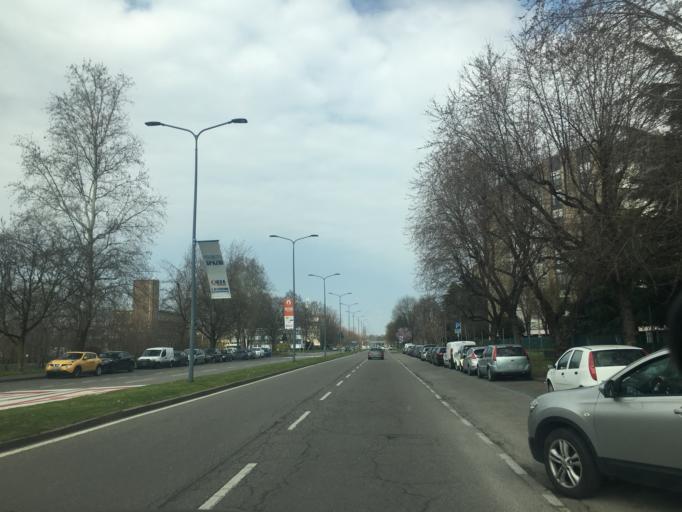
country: IT
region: Lombardy
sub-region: Citta metropolitana di Milano
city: Bresso
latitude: 45.5213
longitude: 9.2055
